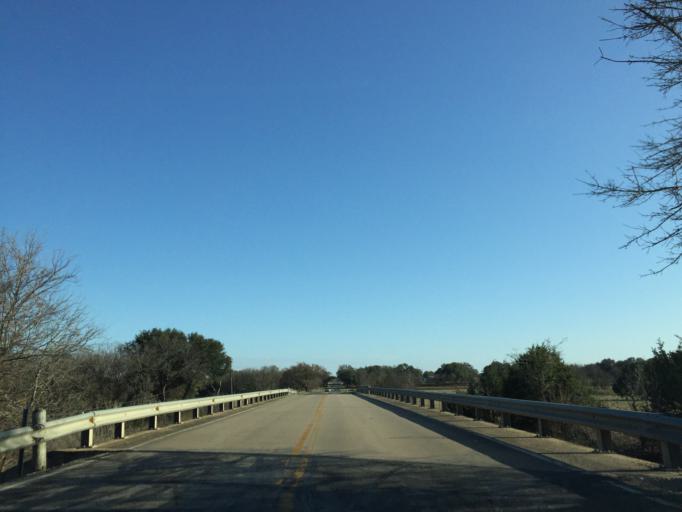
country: US
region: Texas
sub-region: Williamson County
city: Florence
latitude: 30.7754
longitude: -97.7908
